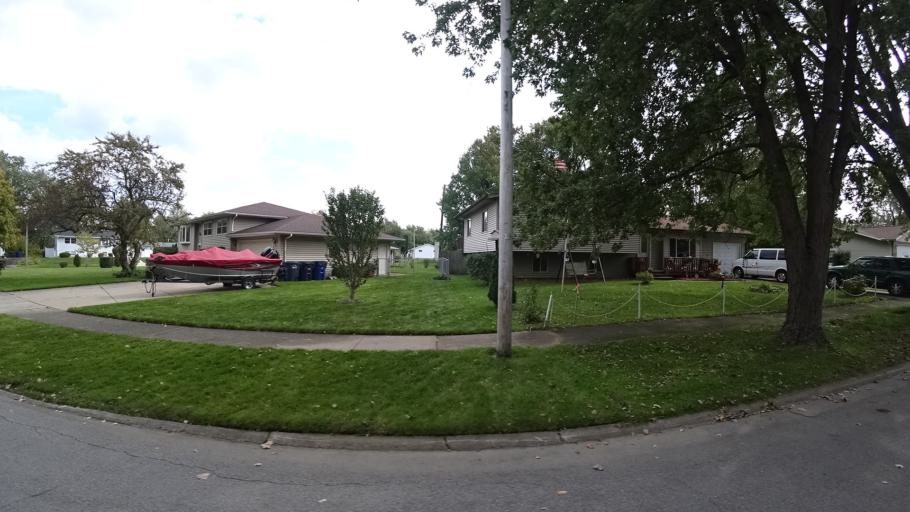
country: US
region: Indiana
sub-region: LaPorte County
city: Michigan City
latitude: 41.6731
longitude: -86.9025
